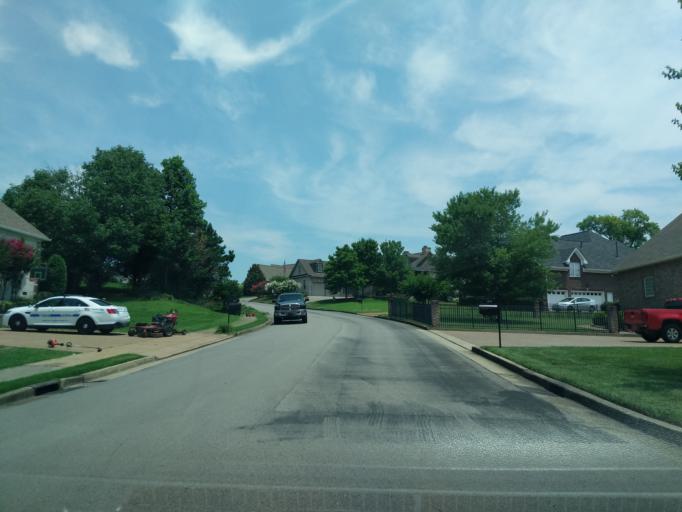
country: US
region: Tennessee
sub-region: Davidson County
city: Lakewood
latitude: 36.2305
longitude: -86.6300
